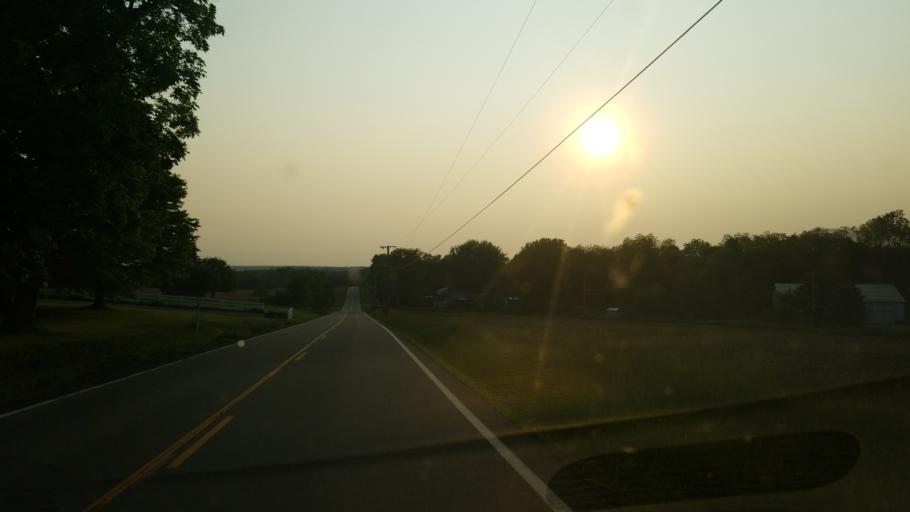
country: US
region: Ohio
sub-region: Ashland County
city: Ashland
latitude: 40.9327
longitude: -82.3054
